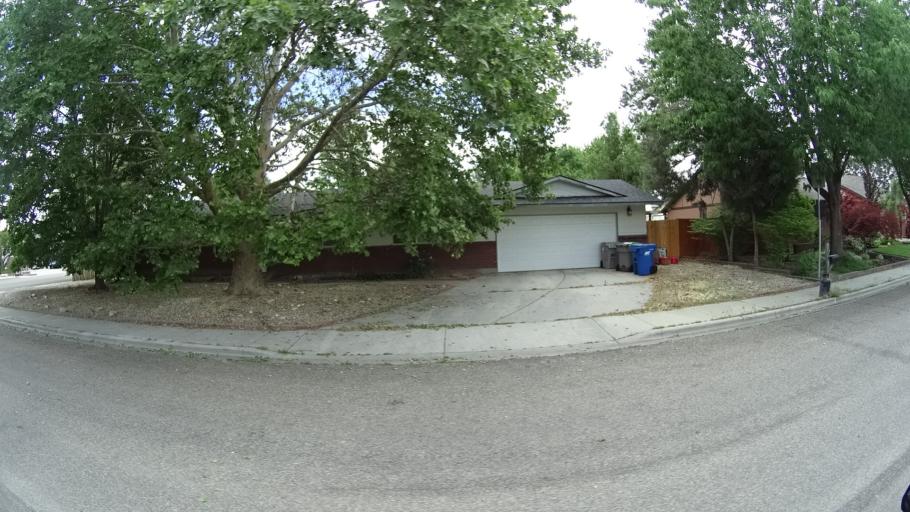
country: US
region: Idaho
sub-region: Ada County
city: Eagle
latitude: 43.6409
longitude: -116.3244
